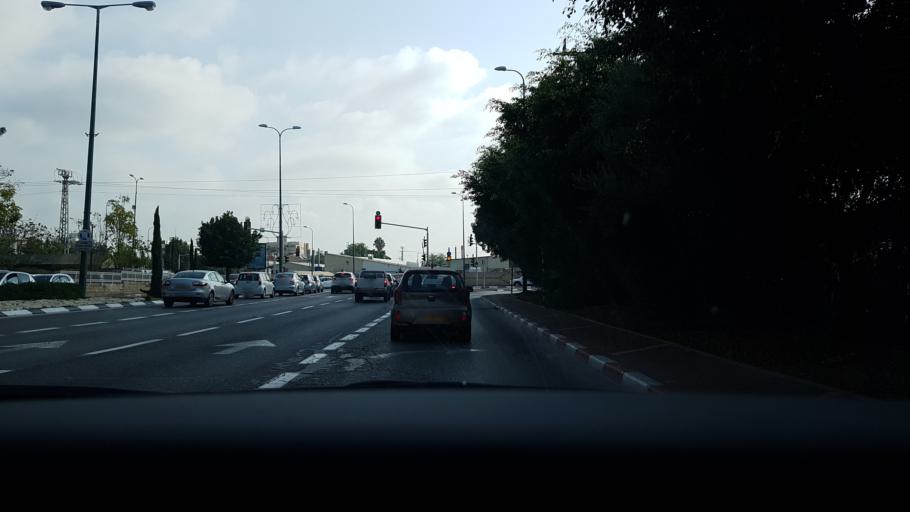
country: IL
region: Central District
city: Ness Ziona
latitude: 31.9241
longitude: 34.7968
